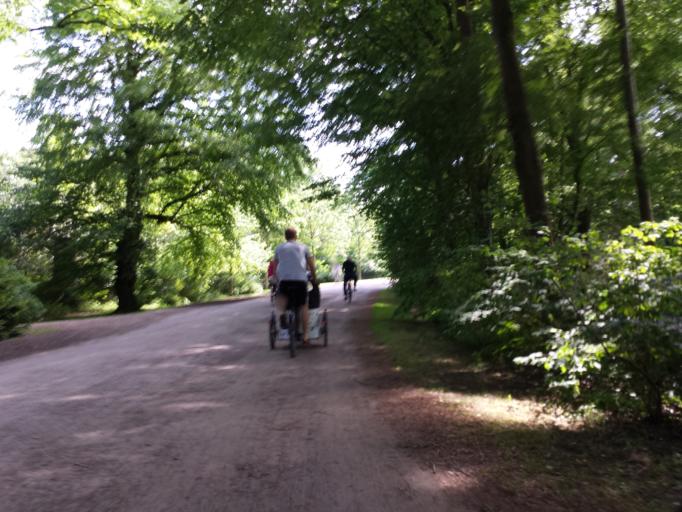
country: DE
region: Bremen
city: Bremen
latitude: 53.0953
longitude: 8.8322
